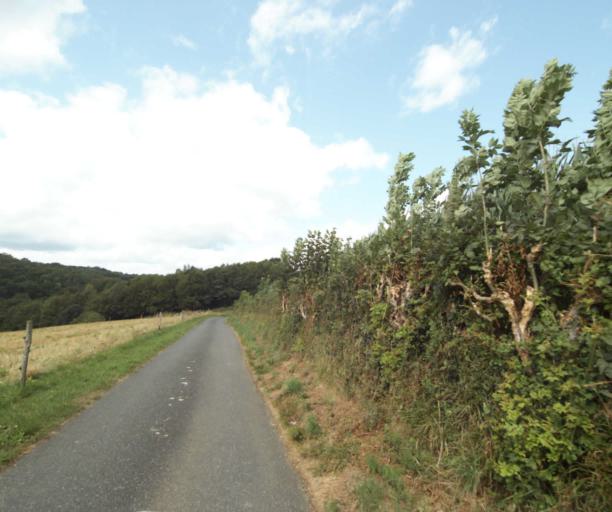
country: FR
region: Limousin
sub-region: Departement de la Correze
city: Sainte-Fortunade
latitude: 45.2120
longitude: 1.8075
